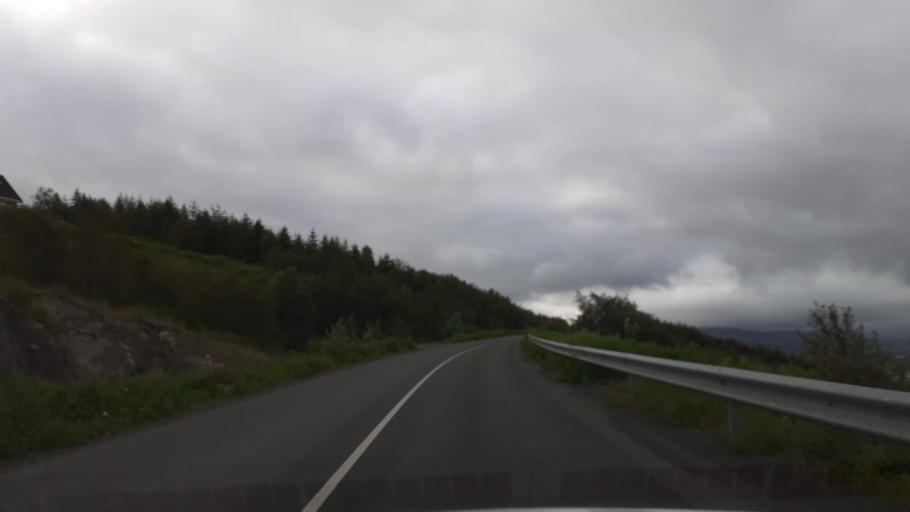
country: IS
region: Northeast
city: Akureyri
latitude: 65.6832
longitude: -18.0434
